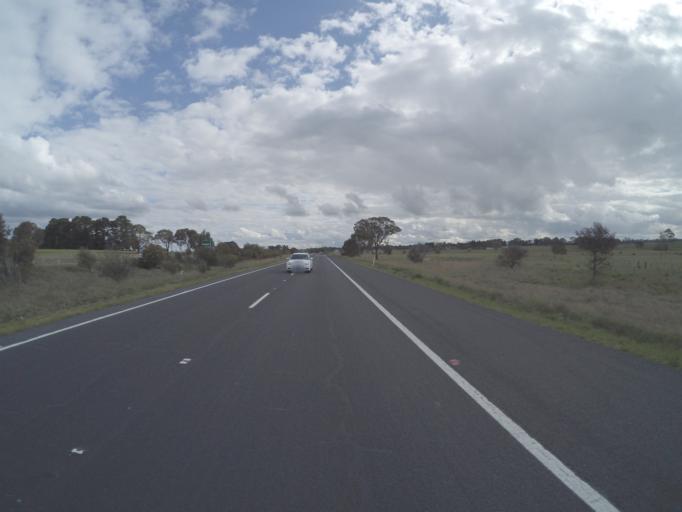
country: AU
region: New South Wales
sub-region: Goulburn Mulwaree
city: Goulburn
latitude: -34.7884
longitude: 149.6240
